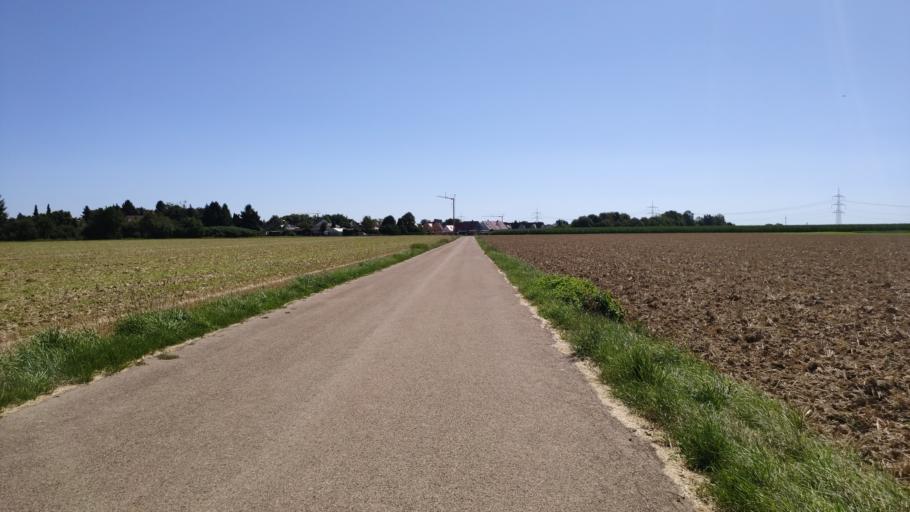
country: DE
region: Bavaria
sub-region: Swabia
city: Oberottmarshausen
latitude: 48.2387
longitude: 10.8460
